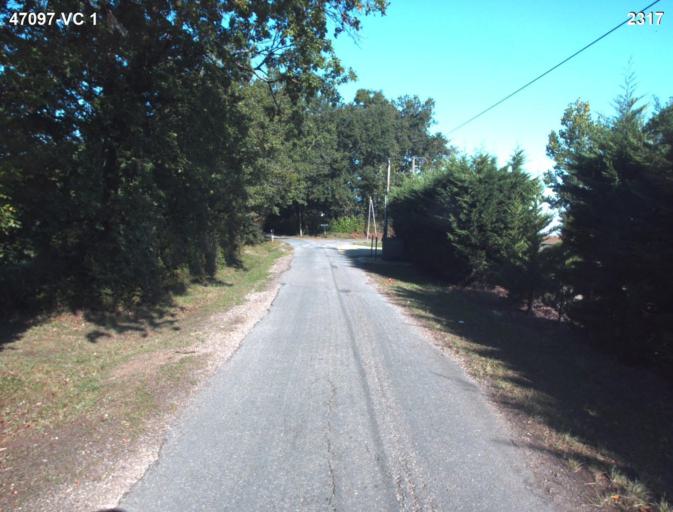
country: FR
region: Aquitaine
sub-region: Departement du Lot-et-Garonne
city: Vianne
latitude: 44.2054
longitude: 0.3581
